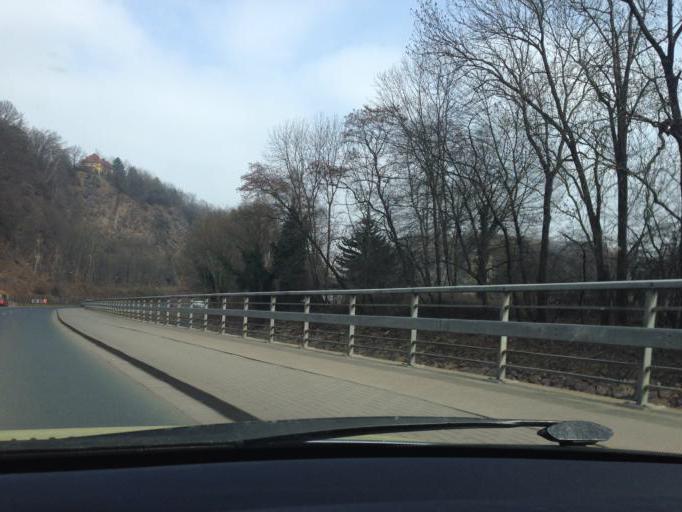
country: DE
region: Saxony
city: Freital
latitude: 51.0200
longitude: 13.6785
